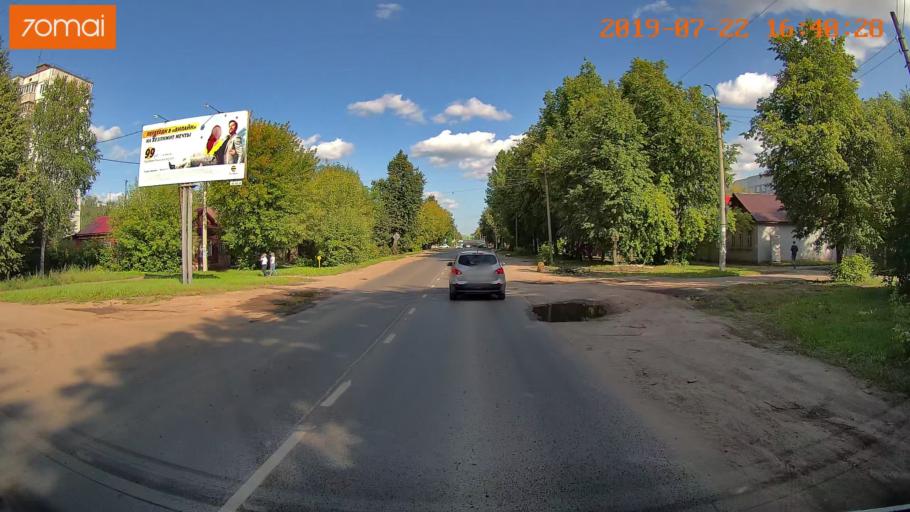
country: RU
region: Ivanovo
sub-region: Gorod Ivanovo
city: Ivanovo
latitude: 57.0236
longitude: 40.9575
